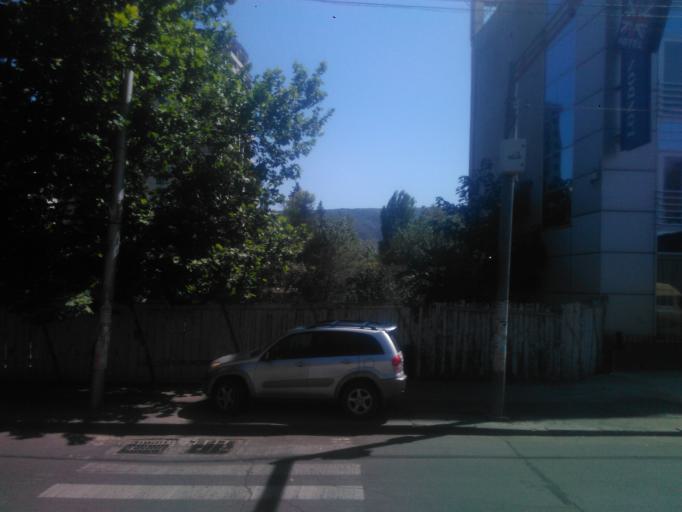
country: GE
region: T'bilisi
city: Tbilisi
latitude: 41.6874
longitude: 44.8313
